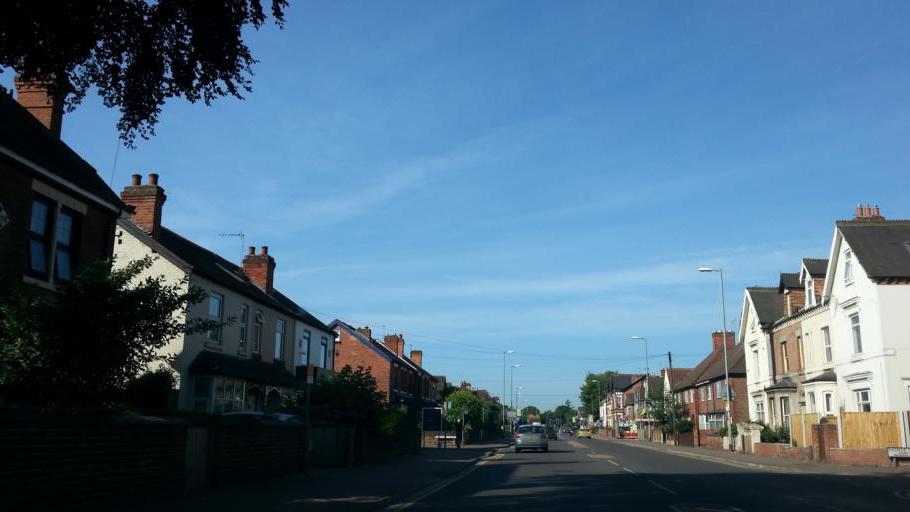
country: GB
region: England
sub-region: Nottinghamshire
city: Gotham
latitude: 52.9243
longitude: -1.2077
